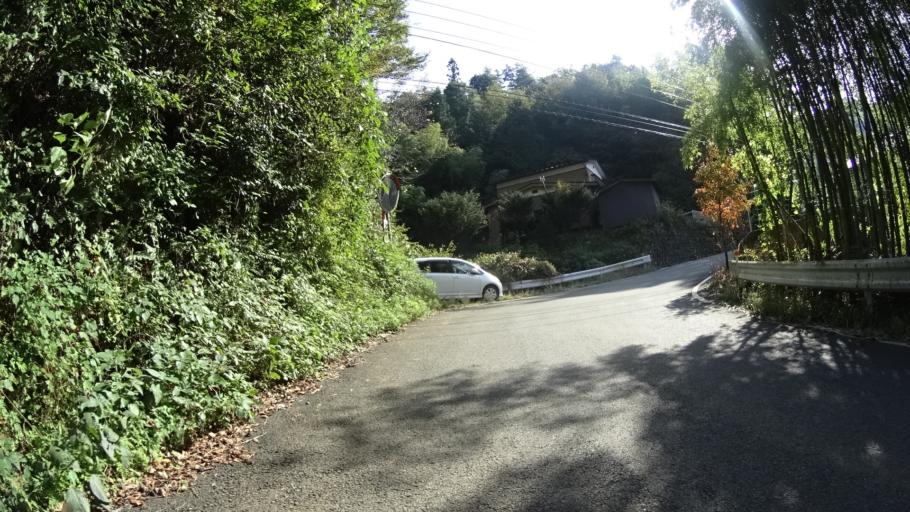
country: JP
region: Yamanashi
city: Otsuki
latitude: 35.5855
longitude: 138.9684
